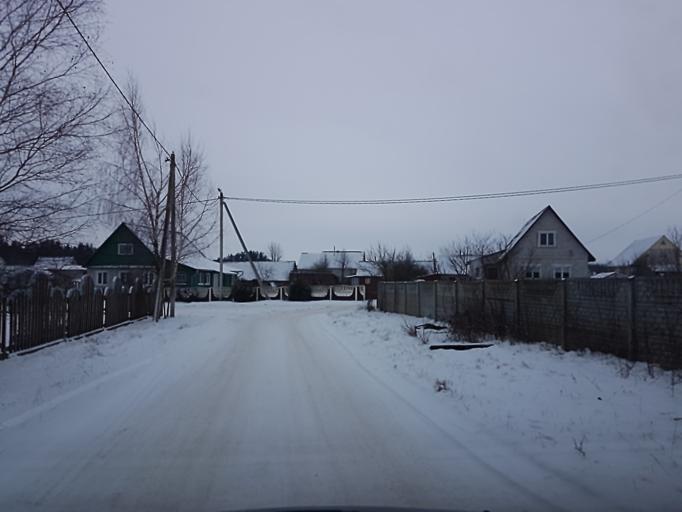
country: BY
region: Minsk
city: Rakaw
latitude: 53.9627
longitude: 27.0429
